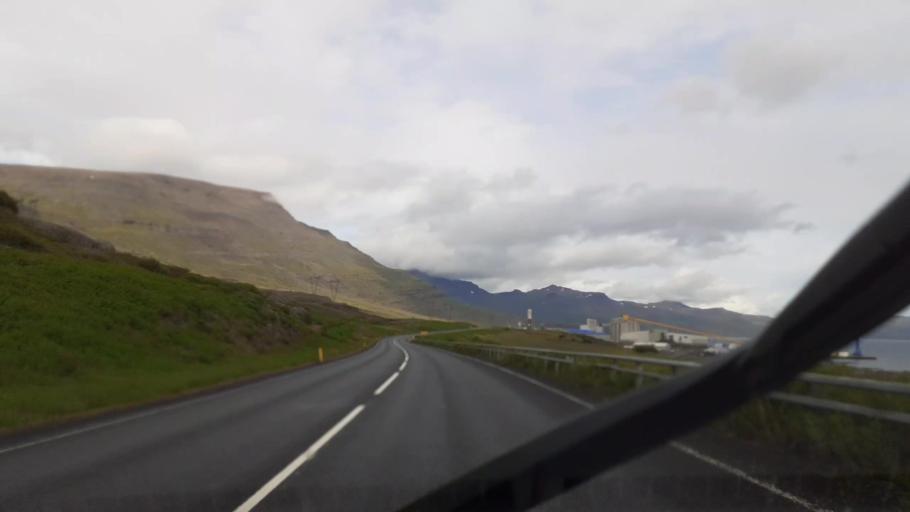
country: IS
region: East
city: Reydarfjoerdur
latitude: 65.0278
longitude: -14.1426
